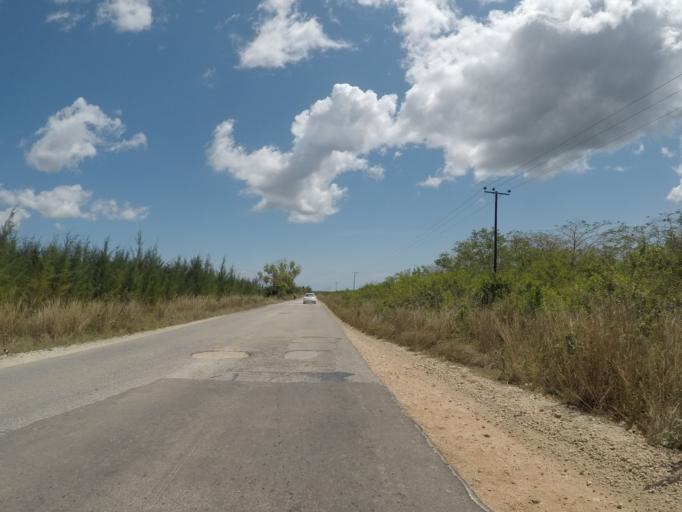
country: TZ
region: Zanzibar Central/South
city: Nganane
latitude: -6.2731
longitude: 39.4924
